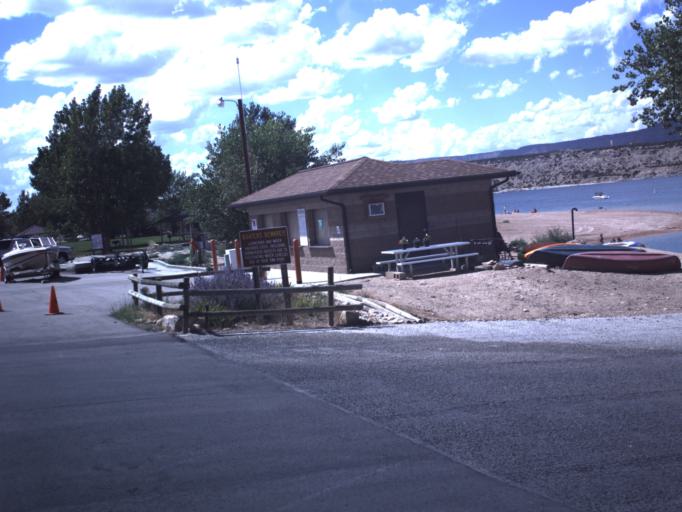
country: US
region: Utah
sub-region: Duchesne County
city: Duchesne
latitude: 40.1912
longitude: -110.4560
